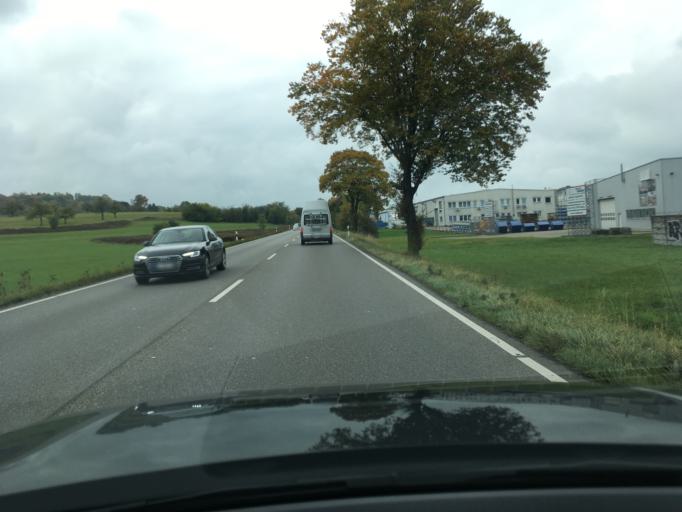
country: DE
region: Baden-Wuerttemberg
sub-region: Tuebingen Region
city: Ofterdingen
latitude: 48.4281
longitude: 9.0479
